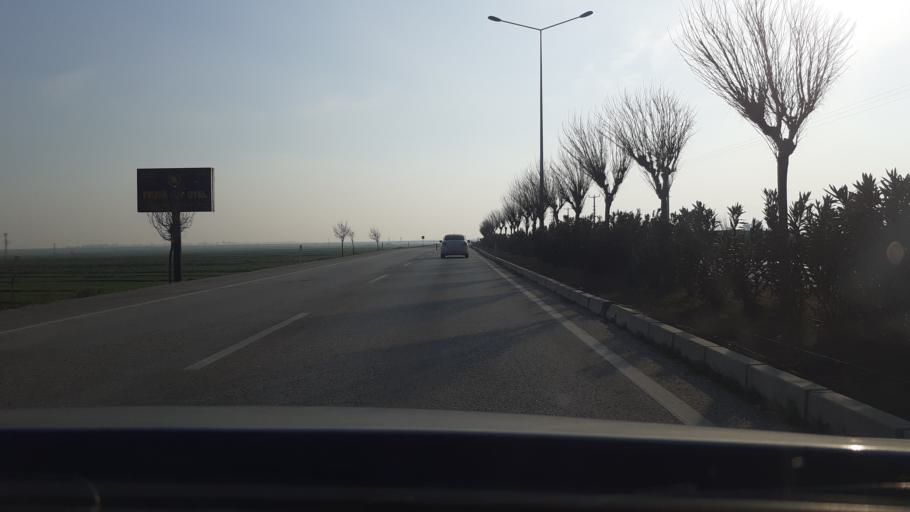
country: TR
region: Hatay
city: Serinyol
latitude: 36.3711
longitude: 36.2479
